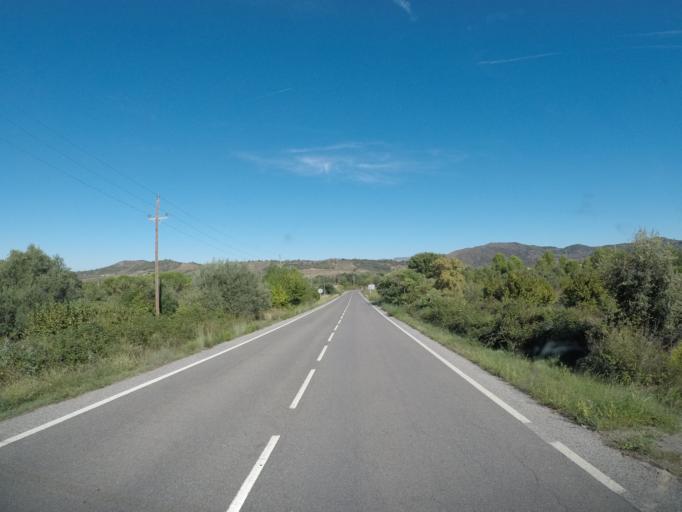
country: ES
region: Catalonia
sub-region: Provincia de Tarragona
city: Falset
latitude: 41.1480
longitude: 0.8191
